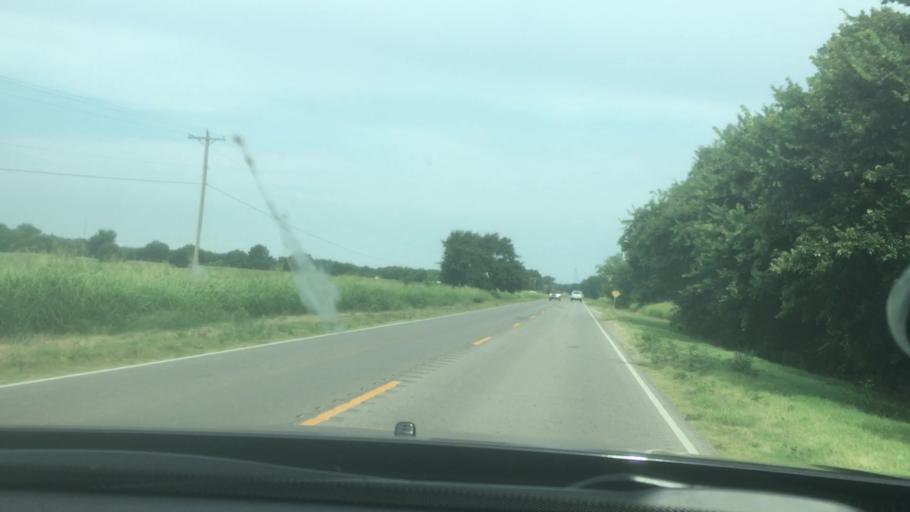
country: US
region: Oklahoma
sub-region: Garvin County
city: Maysville
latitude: 34.8143
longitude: -97.3892
